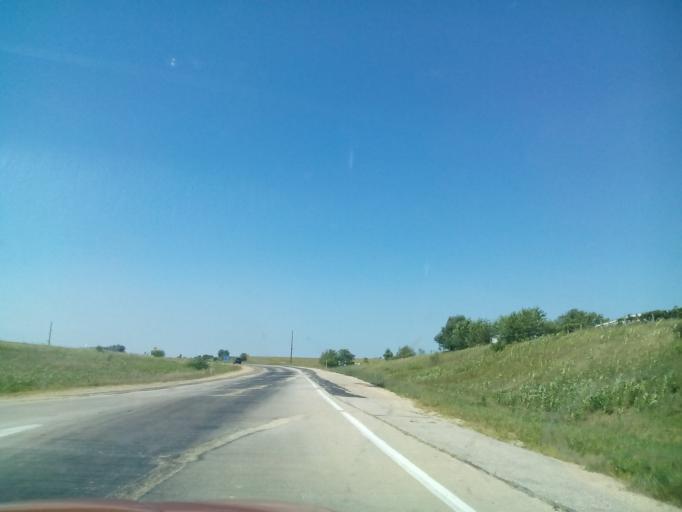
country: US
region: Wisconsin
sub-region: Green County
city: Monroe
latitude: 42.6180
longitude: -89.6371
